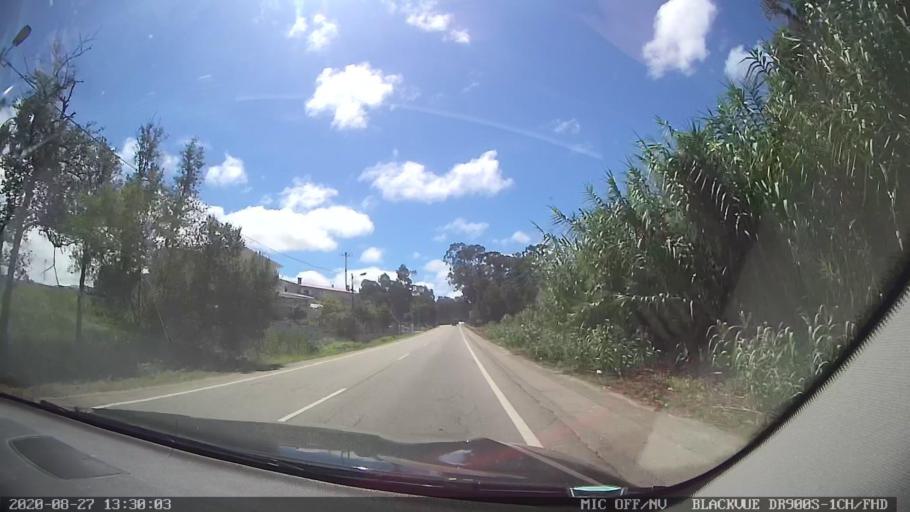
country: PT
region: Aveiro
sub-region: Vagos
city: Vagos
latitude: 40.5077
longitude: -8.6780
